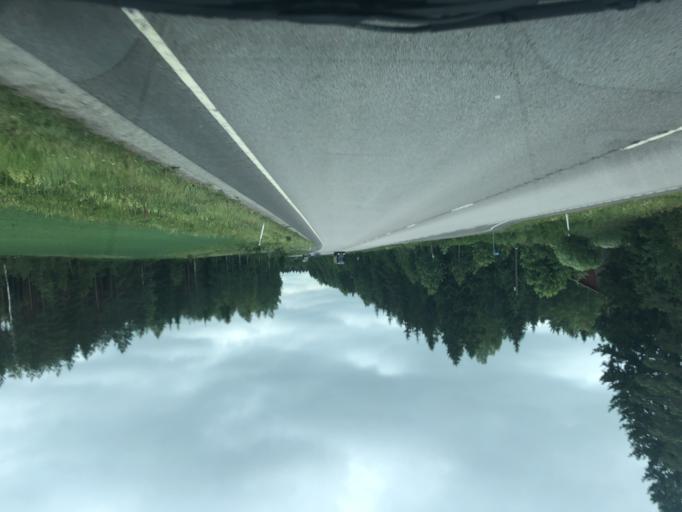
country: FI
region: Uusimaa
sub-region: Loviisa
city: Lapinjaervi
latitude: 60.6762
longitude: 26.2548
